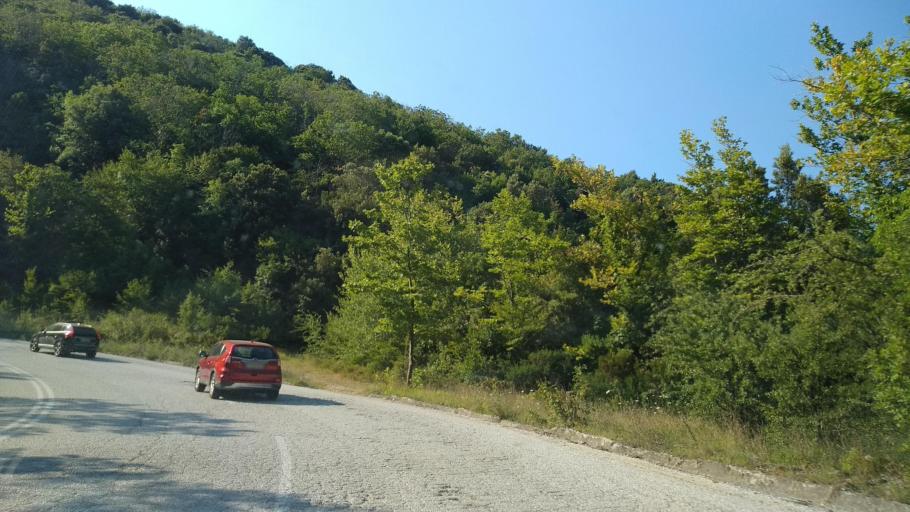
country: GR
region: Central Macedonia
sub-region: Nomos Chalkidikis
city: Stratonion
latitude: 40.5471
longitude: 23.8215
